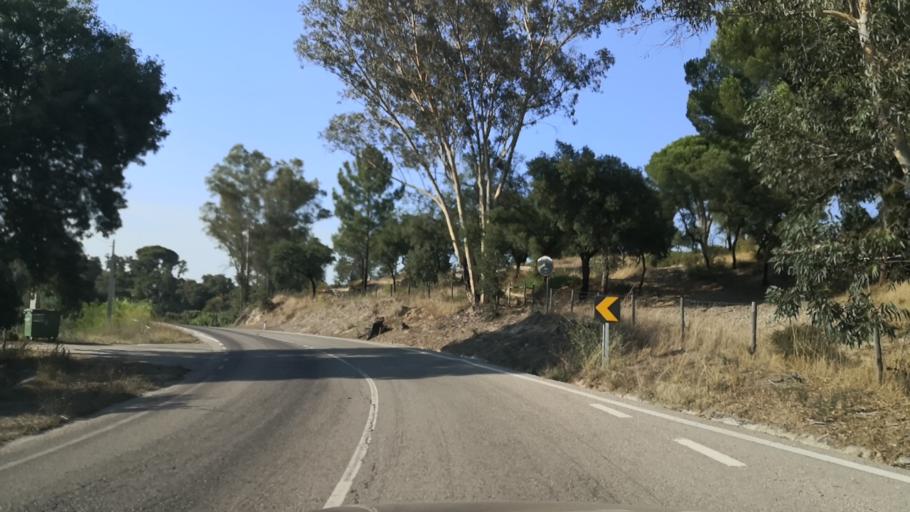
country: PT
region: Santarem
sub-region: Coruche
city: Coruche
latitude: 39.0572
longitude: -8.5659
